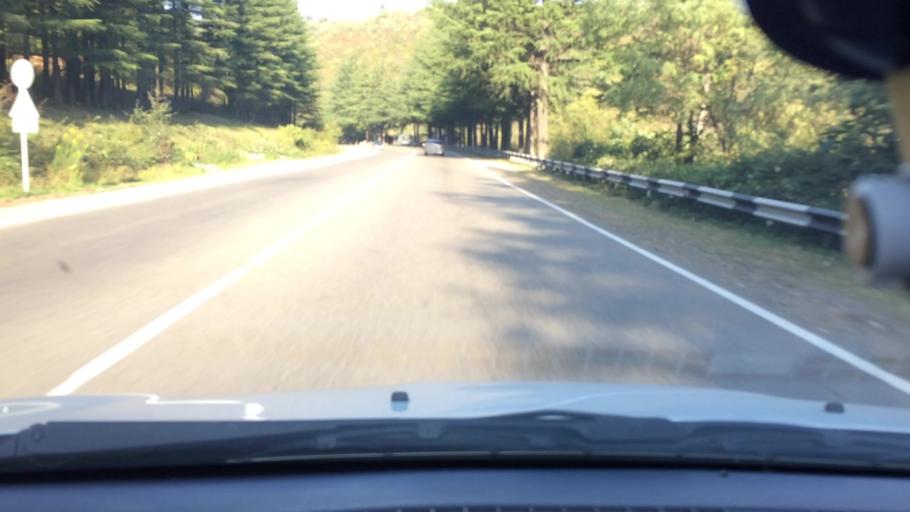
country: GE
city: Shorapani
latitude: 42.0944
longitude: 43.1116
